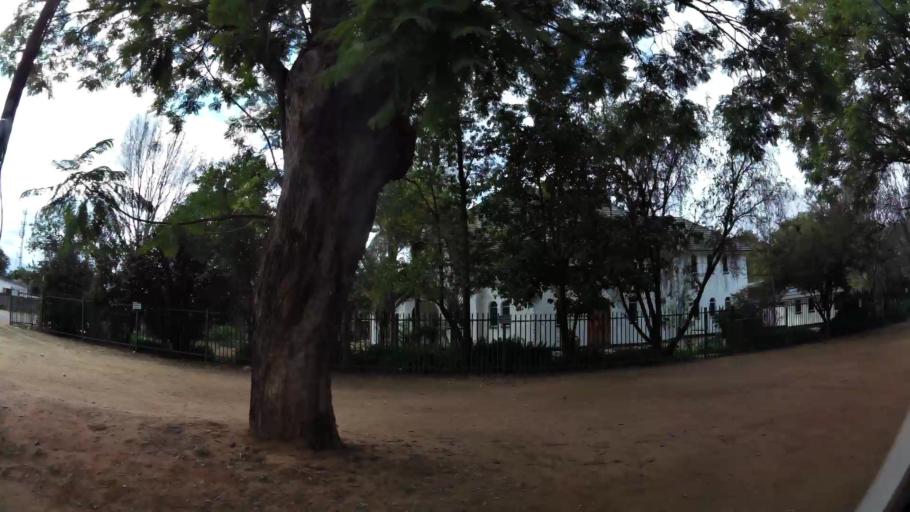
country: ZA
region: Limpopo
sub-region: Waterberg District Municipality
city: Modimolle
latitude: -24.7066
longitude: 28.4090
